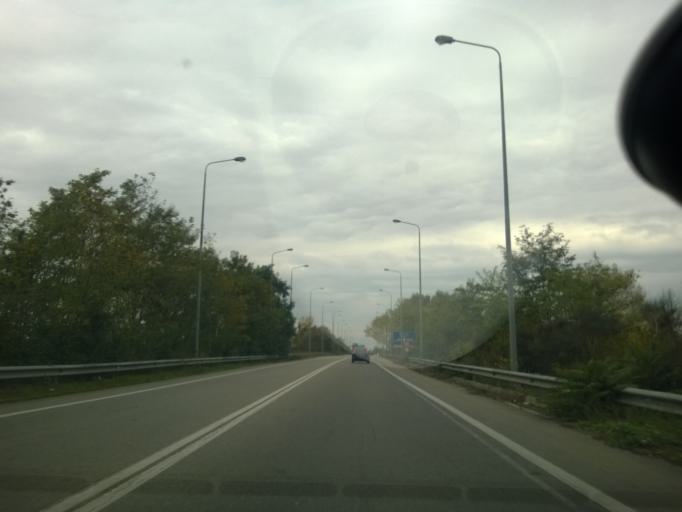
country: GR
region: Central Macedonia
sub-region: Nomos Pellis
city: Karyotissa
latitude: 40.7782
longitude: 22.3192
